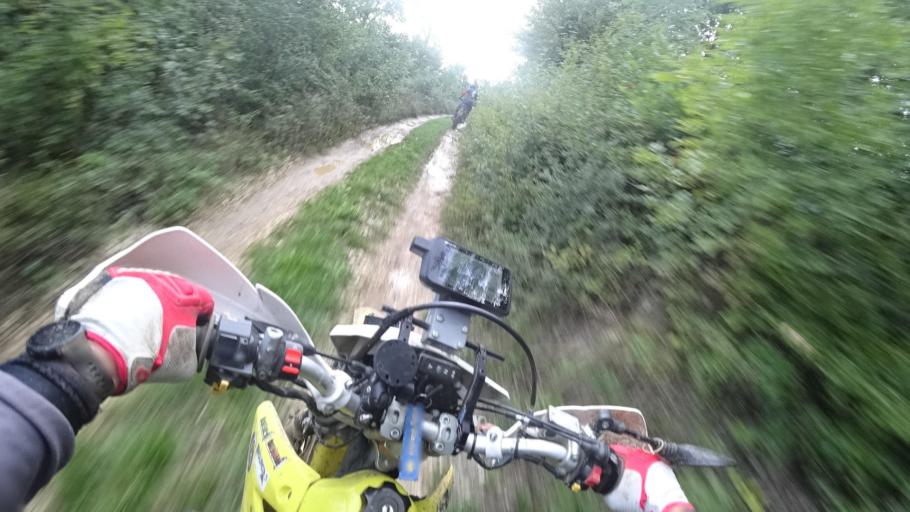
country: BA
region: Republika Srpska
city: Starcevica
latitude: 44.7053
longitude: 17.2203
